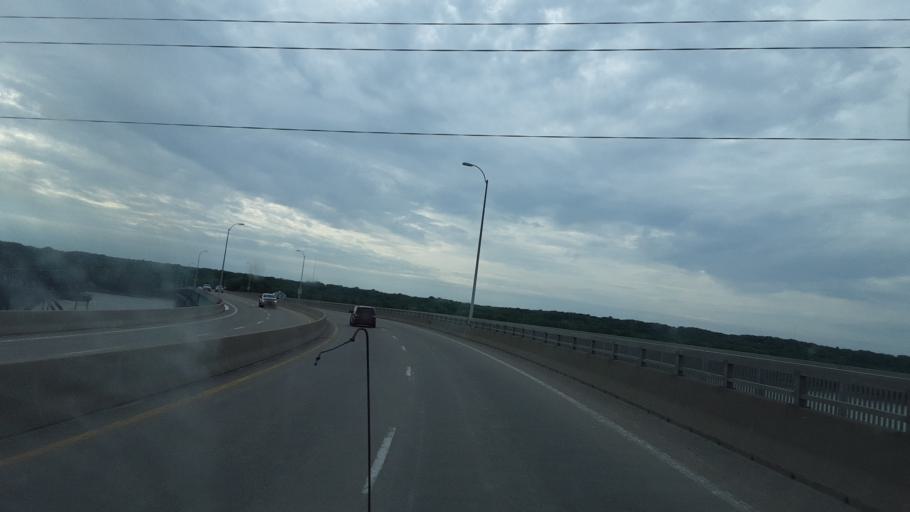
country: US
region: Iowa
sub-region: Lee County
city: Keokuk
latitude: 40.3916
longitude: -91.3790
